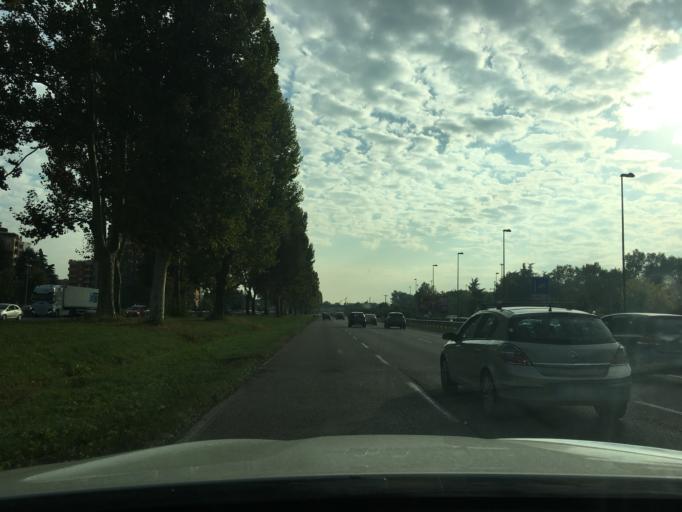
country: IT
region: Lombardy
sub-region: Citta metropolitana di Milano
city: Sesto San Giovanni
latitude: 45.5410
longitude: 9.2201
